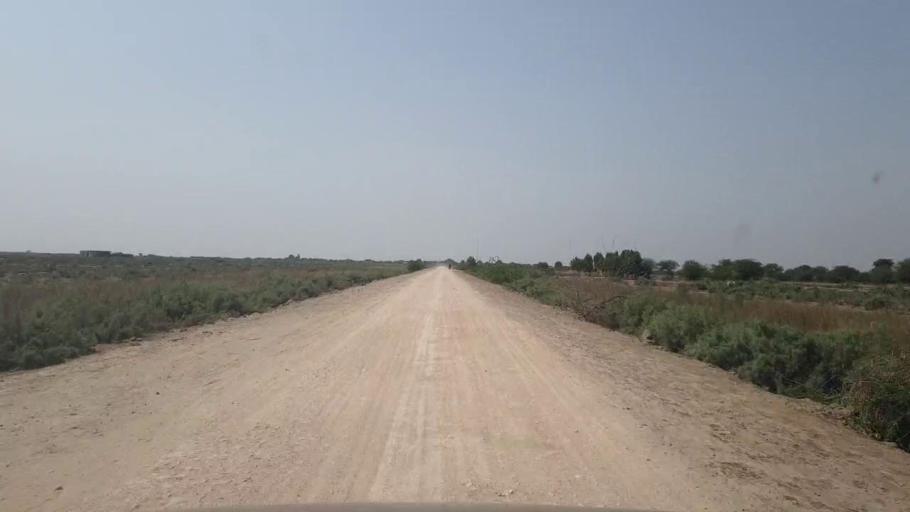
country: PK
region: Sindh
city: Jati
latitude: 24.3653
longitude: 68.5596
